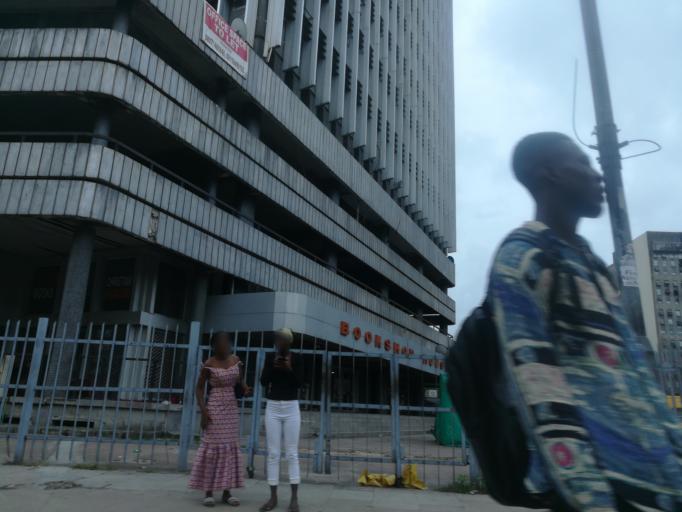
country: NG
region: Lagos
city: Lagos
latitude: 6.4518
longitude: 3.3908
